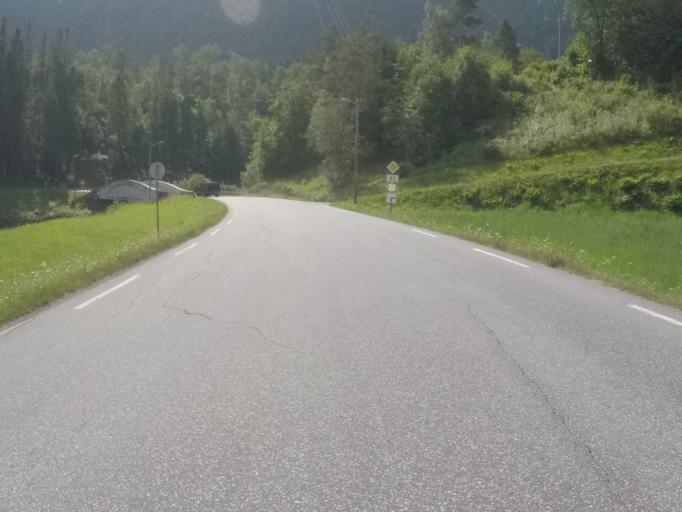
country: NO
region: More og Romsdal
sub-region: Norddal
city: Valldal
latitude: 62.3140
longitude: 7.2896
